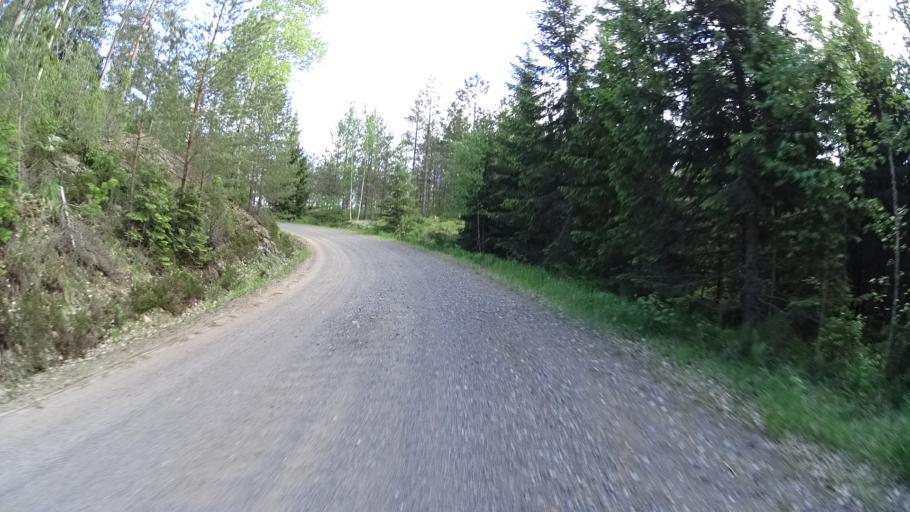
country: FI
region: Uusimaa
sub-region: Raaseporin
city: Pohja
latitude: 60.1567
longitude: 23.4882
